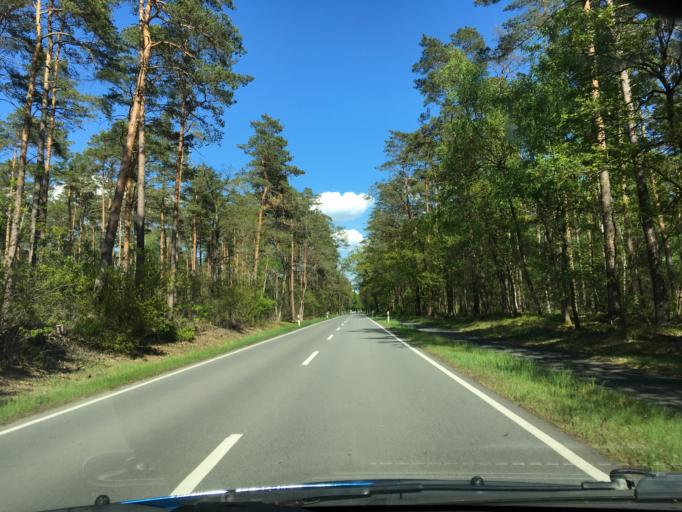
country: DE
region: Lower Saxony
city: Gartow
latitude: 53.0196
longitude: 11.4354
